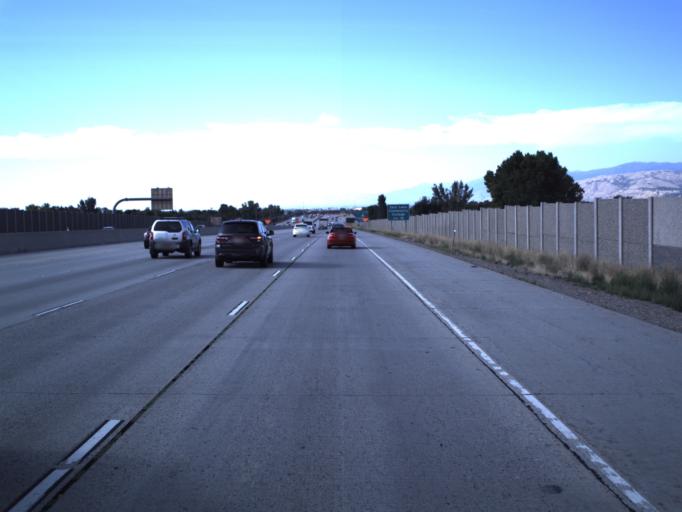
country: US
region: Utah
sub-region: Salt Lake County
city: Taylorsville
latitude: 40.6539
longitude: -111.9524
